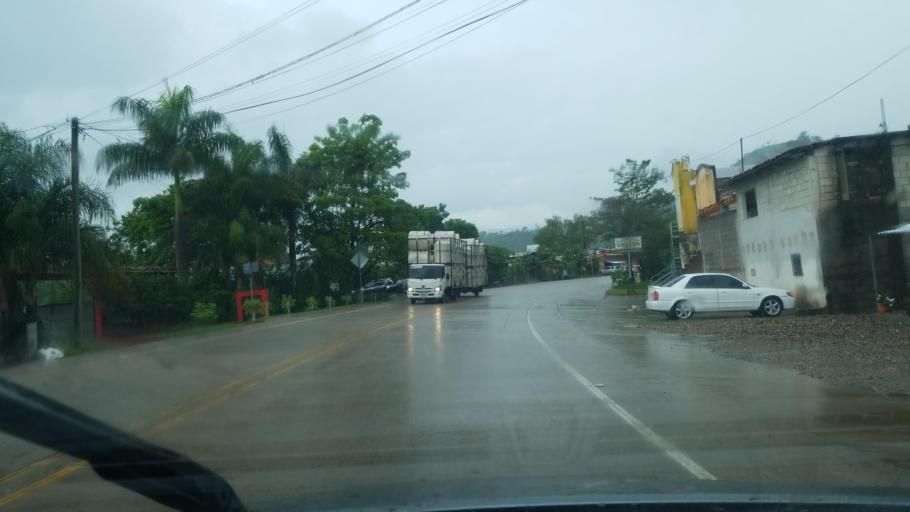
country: HN
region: Copan
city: Copan
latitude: 14.8344
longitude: -89.1583
